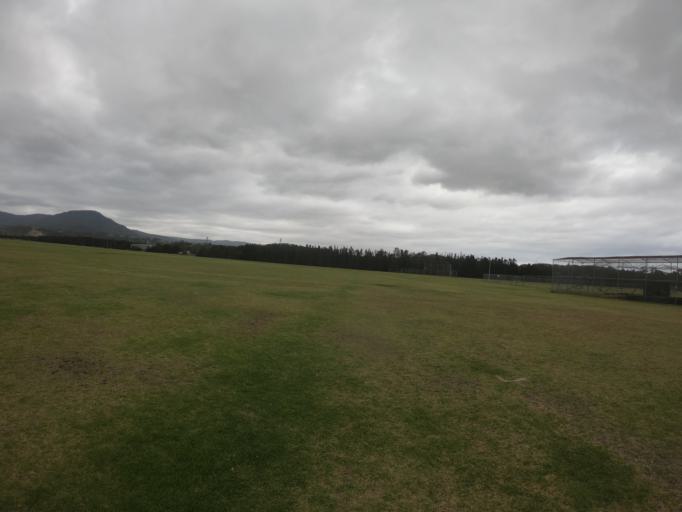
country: AU
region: New South Wales
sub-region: Wollongong
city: Berkeley
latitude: -34.4840
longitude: 150.8365
